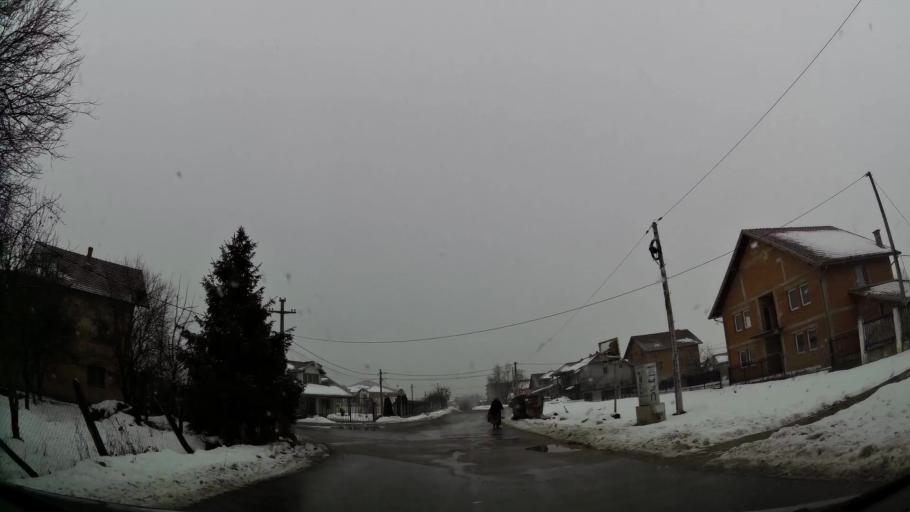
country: RS
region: Central Serbia
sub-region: Belgrade
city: Zemun
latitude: 44.8573
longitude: 20.3302
